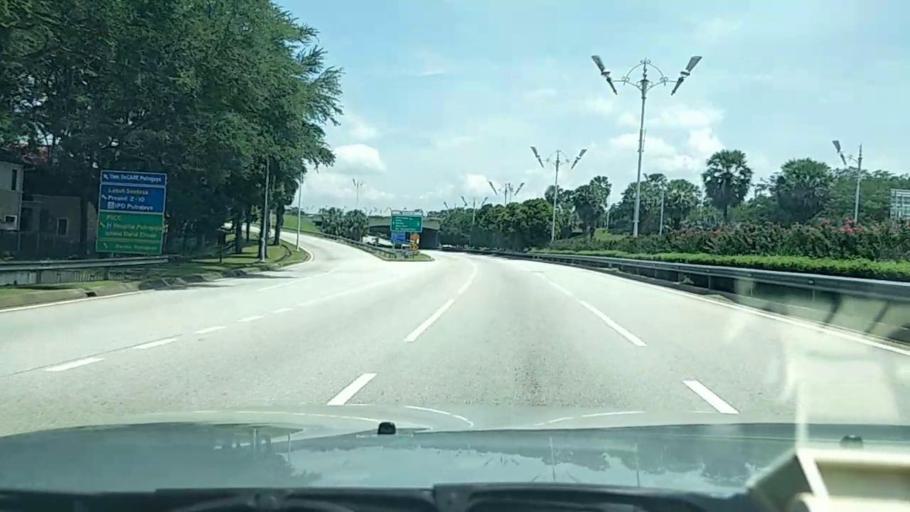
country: MY
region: Putrajaya
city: Putrajaya
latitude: 2.9538
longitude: 101.6849
